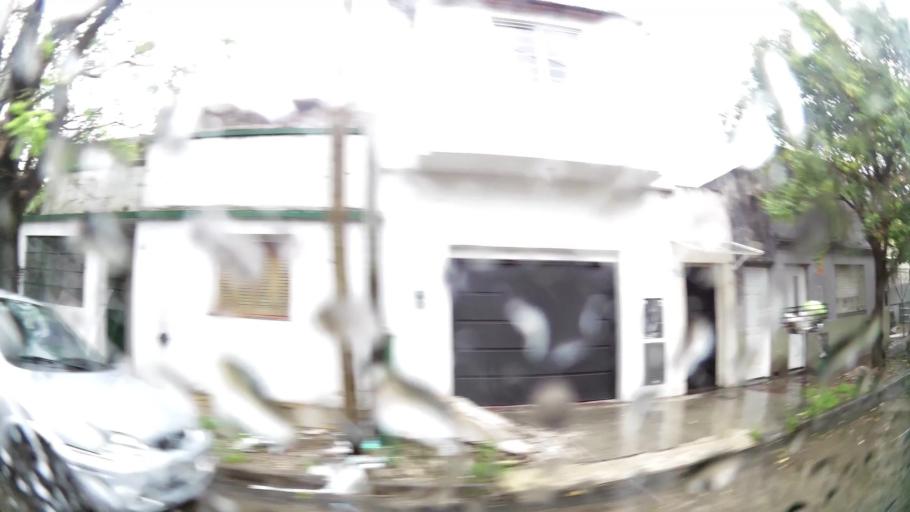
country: AR
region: Buenos Aires
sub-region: Partido de Lanus
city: Lanus
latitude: -34.7163
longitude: -58.4106
